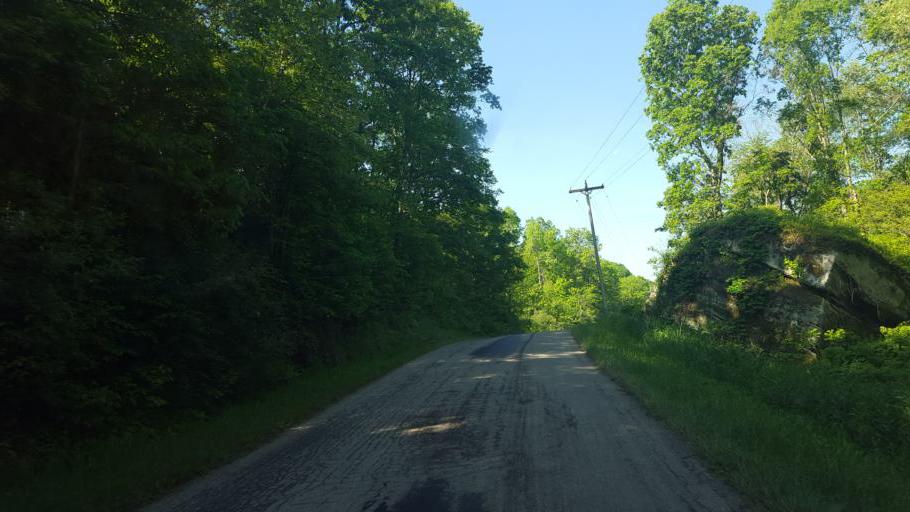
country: US
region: Ohio
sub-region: Jackson County
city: Oak Hill
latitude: 38.9882
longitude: -82.5022
